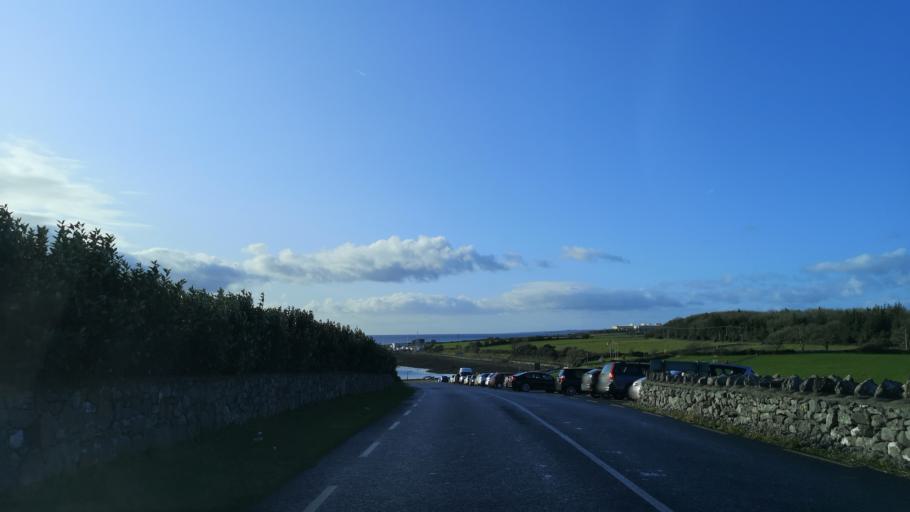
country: IE
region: Connaught
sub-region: County Galway
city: Oranmore
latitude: 53.2457
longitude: -8.9578
